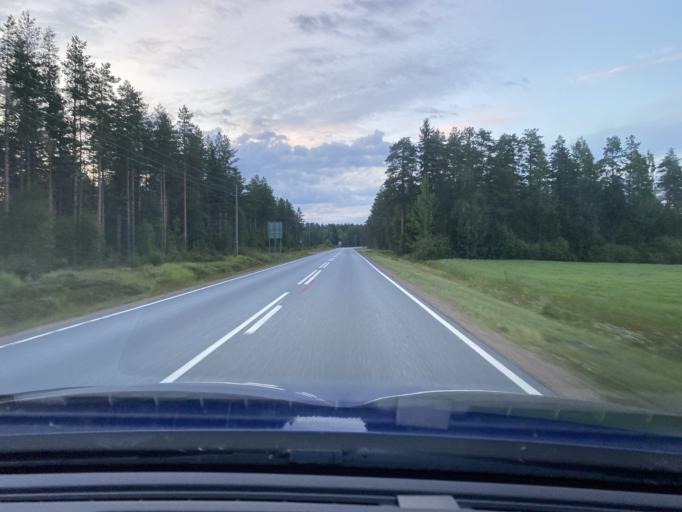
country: FI
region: Satakunta
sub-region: Pohjois-Satakunta
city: Honkajoki
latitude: 62.1530
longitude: 22.2651
